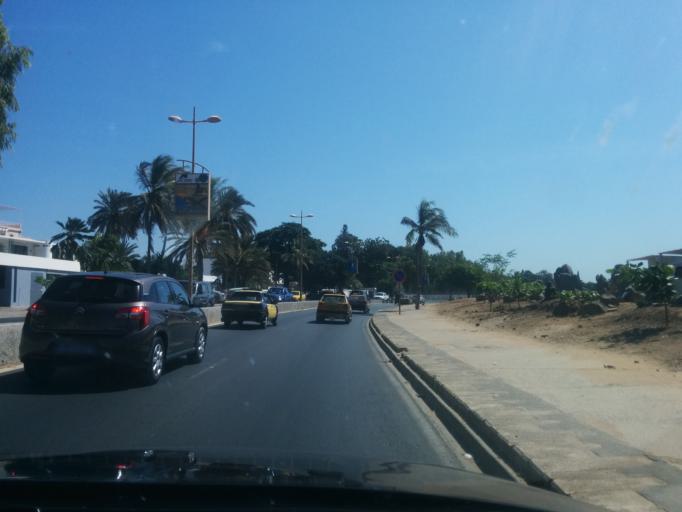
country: SN
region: Dakar
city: Mermoz Boabab
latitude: 14.7002
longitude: -17.4733
